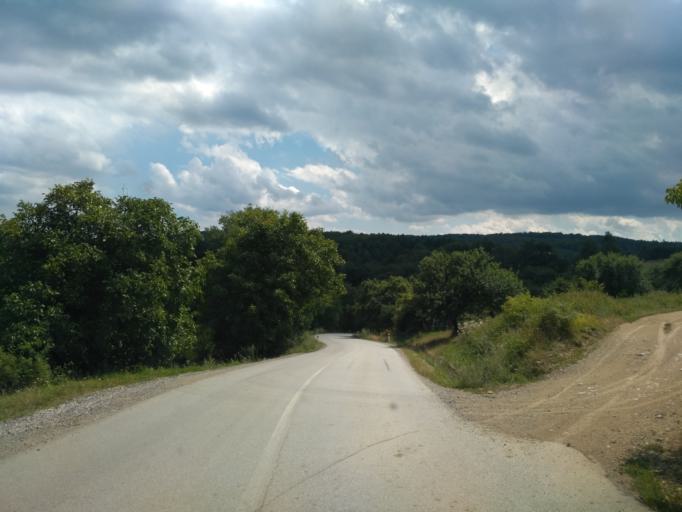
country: SK
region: Kosicky
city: Gelnica
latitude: 48.9264
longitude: 21.0491
